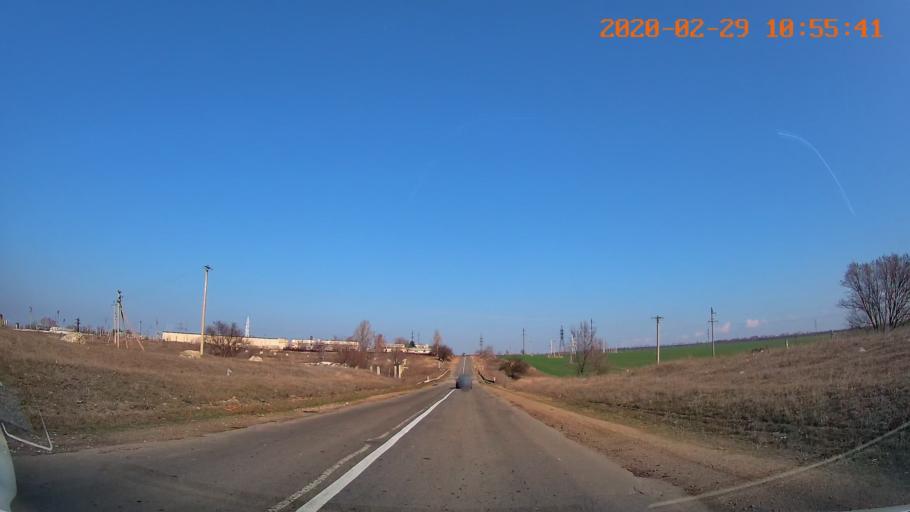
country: MD
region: Telenesti
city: Grigoriopol
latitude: 47.1366
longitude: 29.3254
